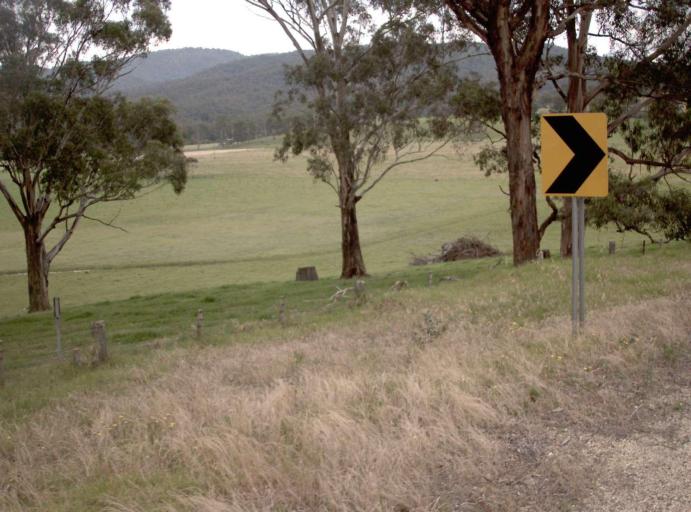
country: AU
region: New South Wales
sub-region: Bombala
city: Bombala
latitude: -37.4827
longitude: 149.1802
